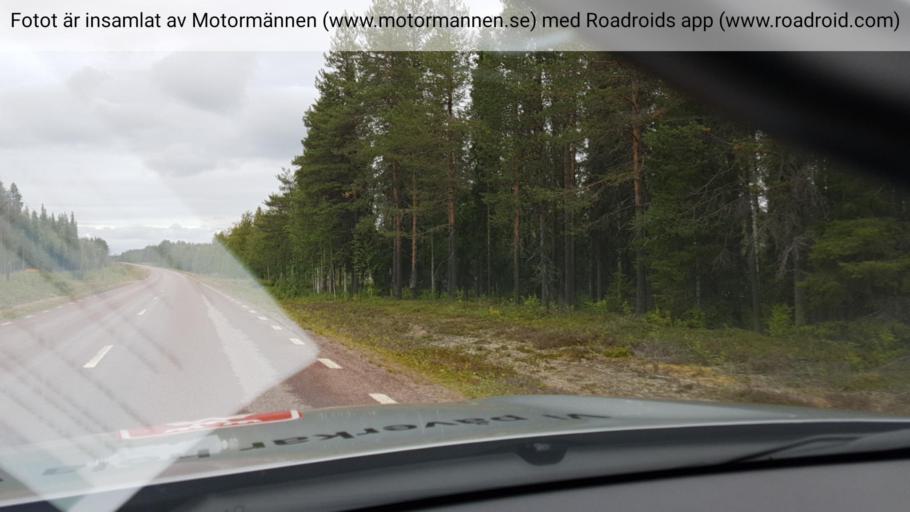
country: SE
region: Norrbotten
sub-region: Pajala Kommun
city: Pajala
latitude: 67.1146
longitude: 22.6035
